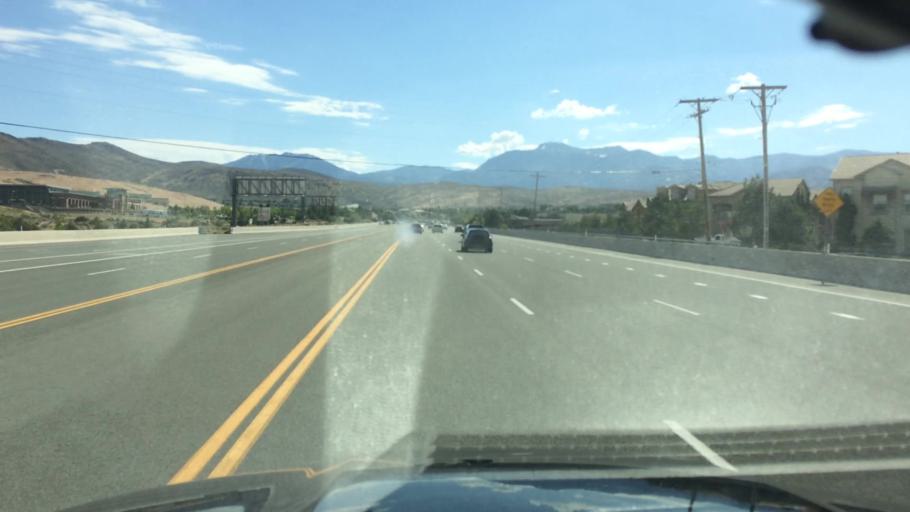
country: US
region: Nevada
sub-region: Washoe County
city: Sparks
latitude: 39.3953
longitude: -119.7617
